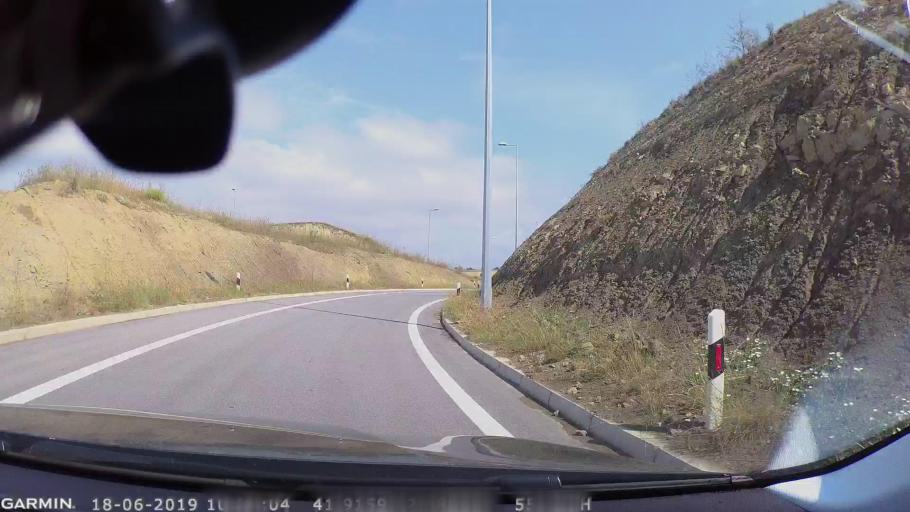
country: MK
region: Sveti Nikole
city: Gorobinci
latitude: 41.9143
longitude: 21.8871
